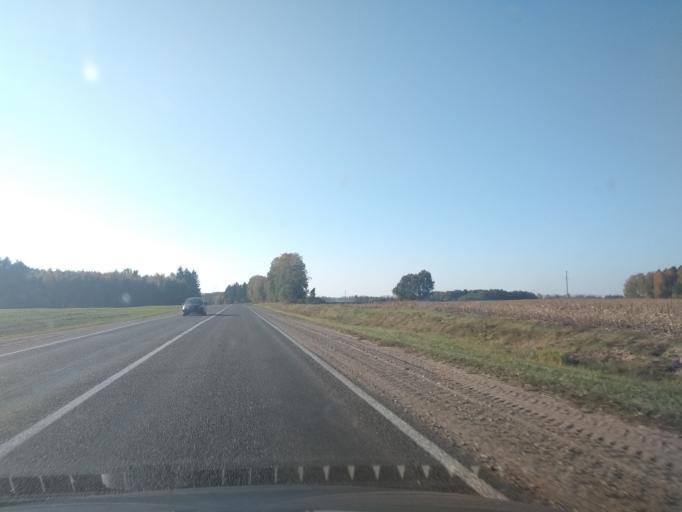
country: BY
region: Grodnenskaya
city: Vyalikaya Byerastavitsa
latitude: 53.1180
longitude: 24.0508
